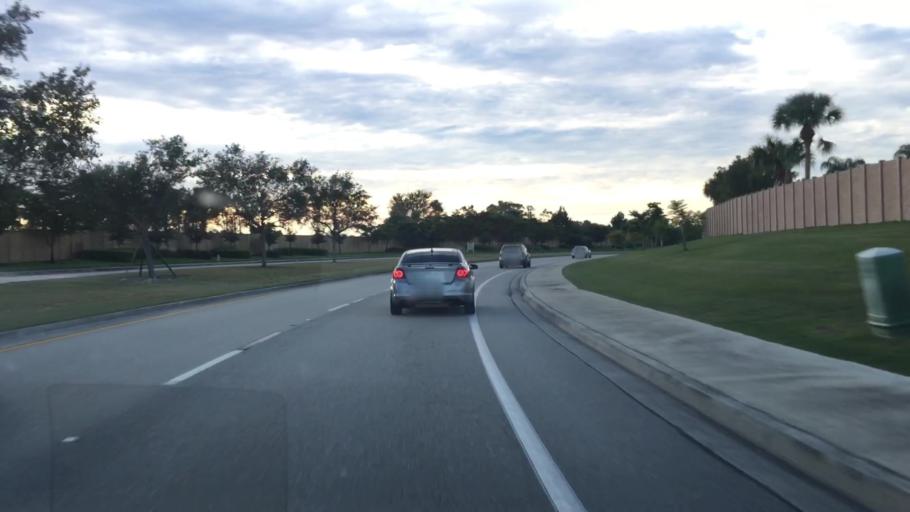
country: US
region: Florida
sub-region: Lee County
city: Gateway
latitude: 26.5929
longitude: -81.7842
